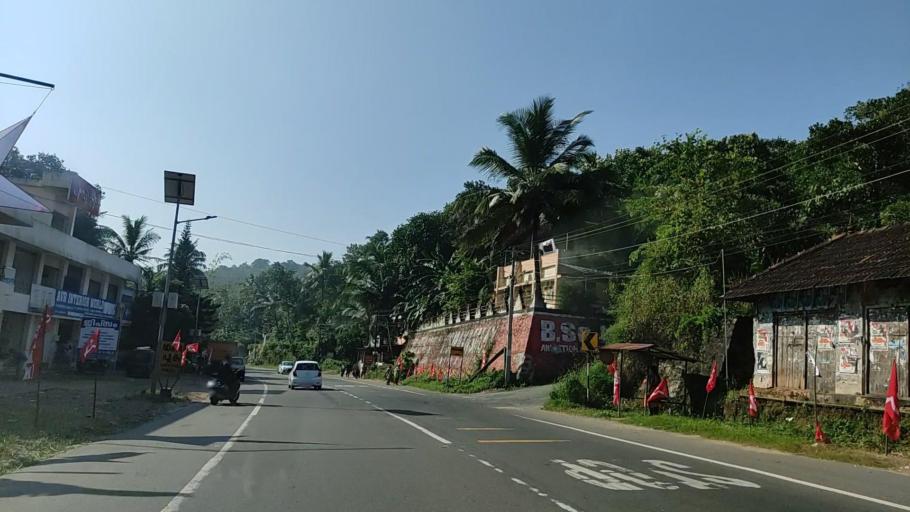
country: IN
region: Kerala
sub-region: Kollam
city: Punalur
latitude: 8.9147
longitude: 76.8532
